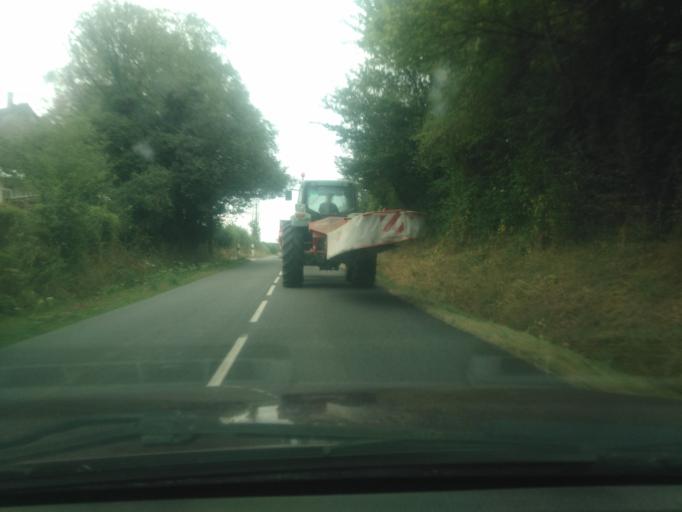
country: FR
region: Bourgogne
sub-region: Departement de la Nievre
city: Dornes
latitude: 46.7719
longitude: 3.3069
